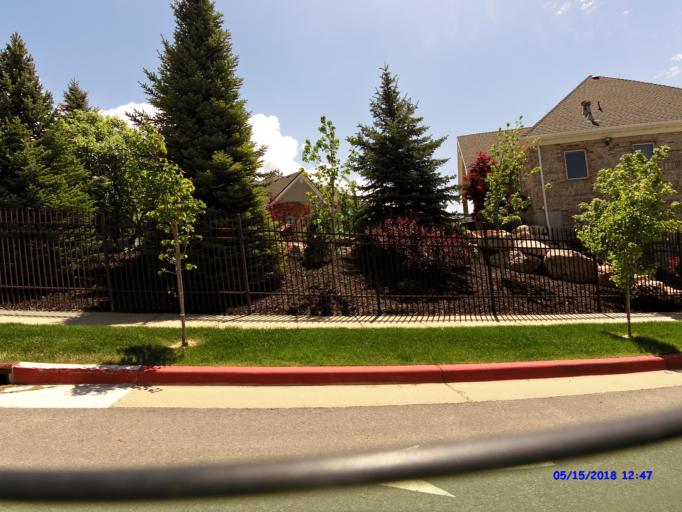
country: US
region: Utah
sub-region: Weber County
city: Uintah
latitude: 41.1610
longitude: -111.9234
